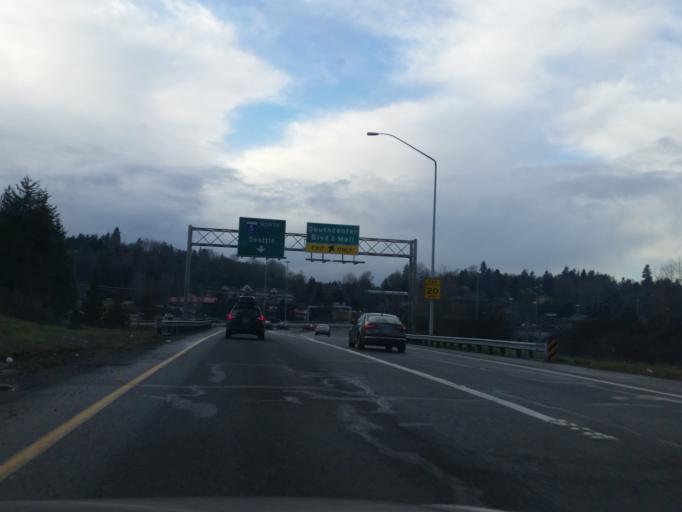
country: US
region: Washington
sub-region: King County
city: Tukwila
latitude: 47.4637
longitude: -122.2621
